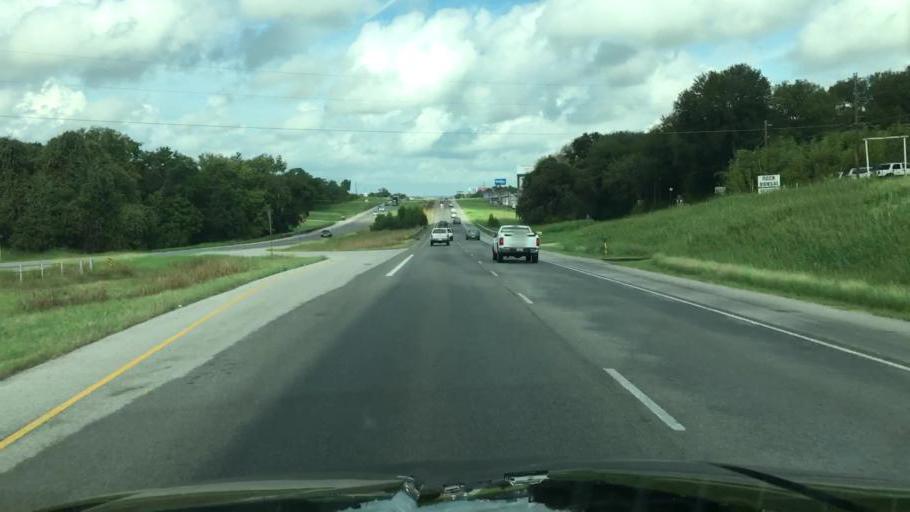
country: US
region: Texas
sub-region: Bastrop County
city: Wyldwood
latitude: 30.1555
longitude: -97.4948
